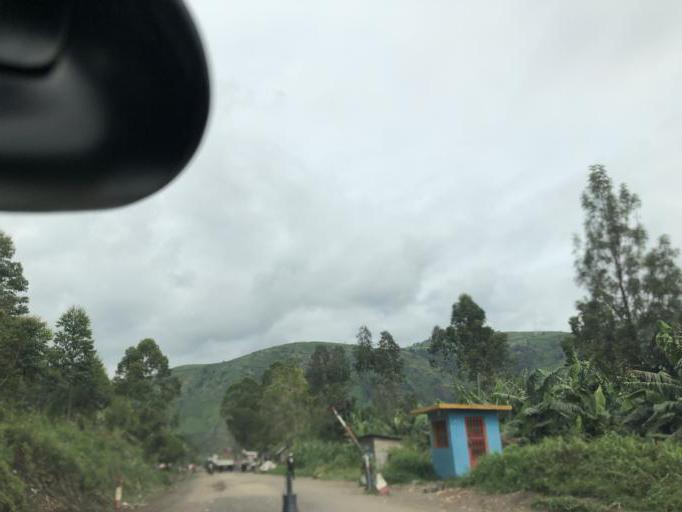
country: CD
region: Nord Kivu
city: Sake
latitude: -1.5704
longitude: 29.0460
